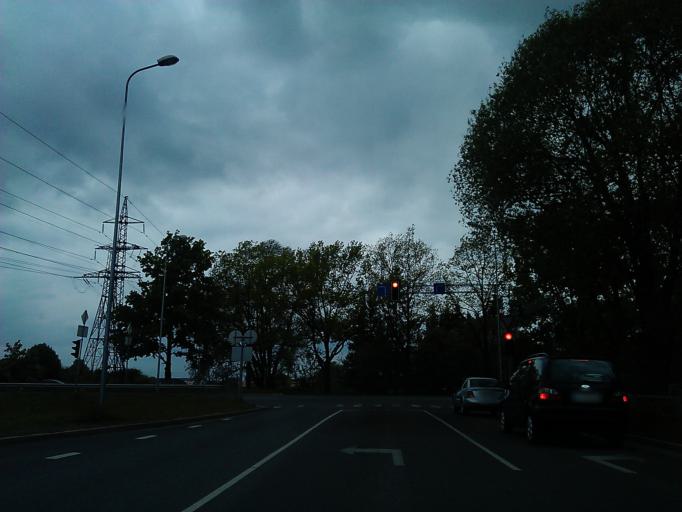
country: LV
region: Marupe
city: Marupe
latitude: 56.8989
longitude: 24.0791
